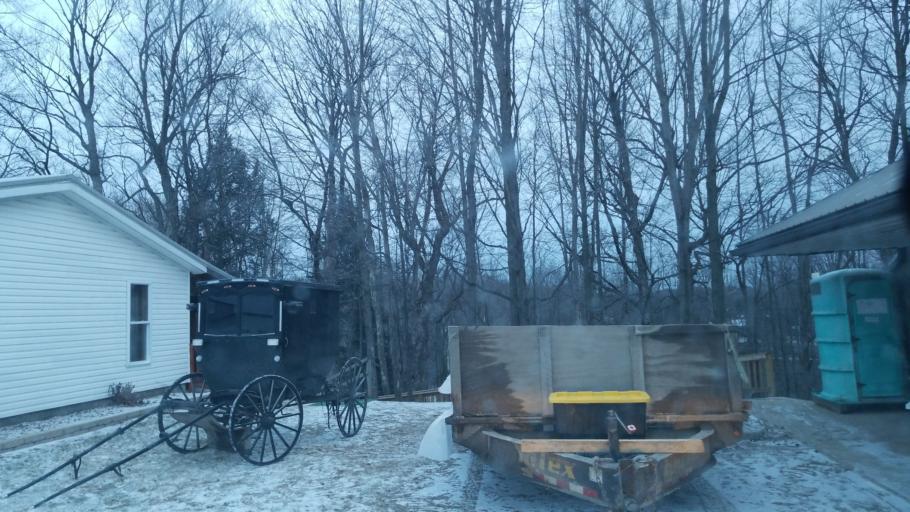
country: US
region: Michigan
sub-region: Osceola County
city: Reed City
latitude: 43.8300
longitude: -85.4313
